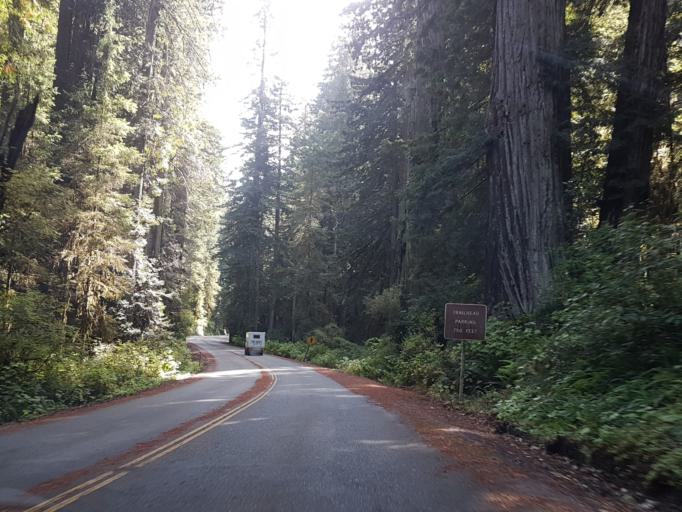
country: US
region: California
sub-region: Del Norte County
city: Bertsch-Oceanview
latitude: 41.4405
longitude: -124.0411
